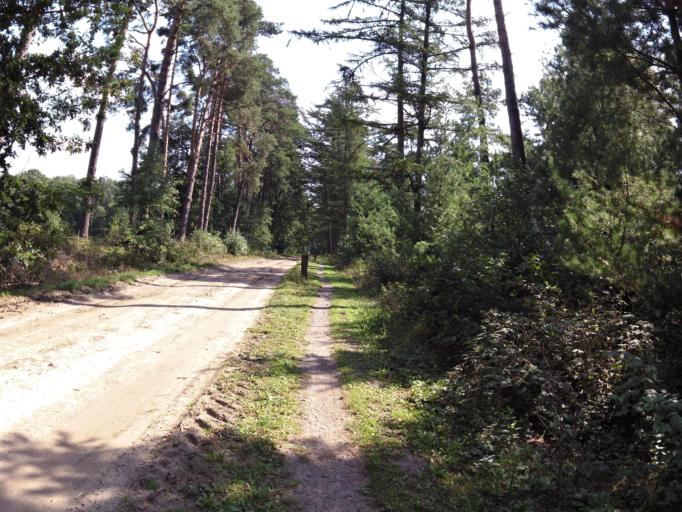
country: DE
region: North Rhine-Westphalia
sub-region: Regierungsbezirk Munster
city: Ahaus
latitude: 52.0242
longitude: 6.9960
